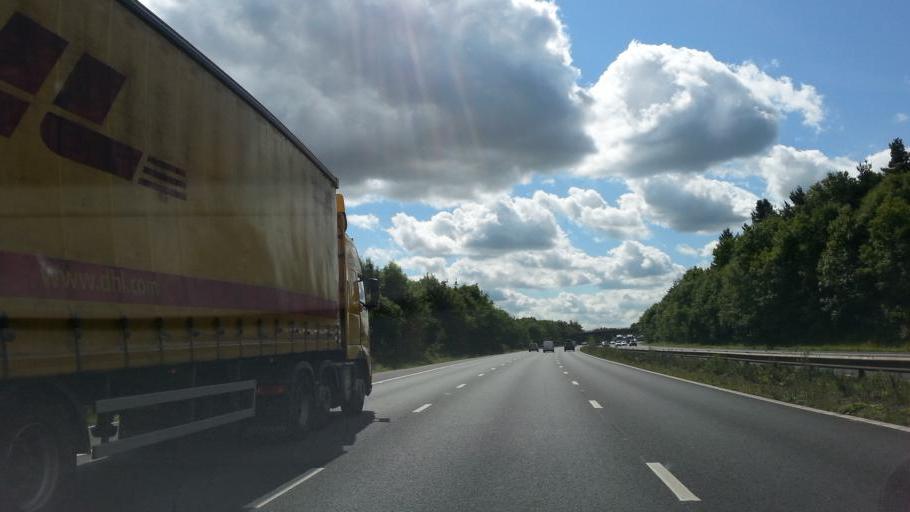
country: GB
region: England
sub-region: Leicestershire
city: Cosby
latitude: 52.5315
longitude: -1.1768
